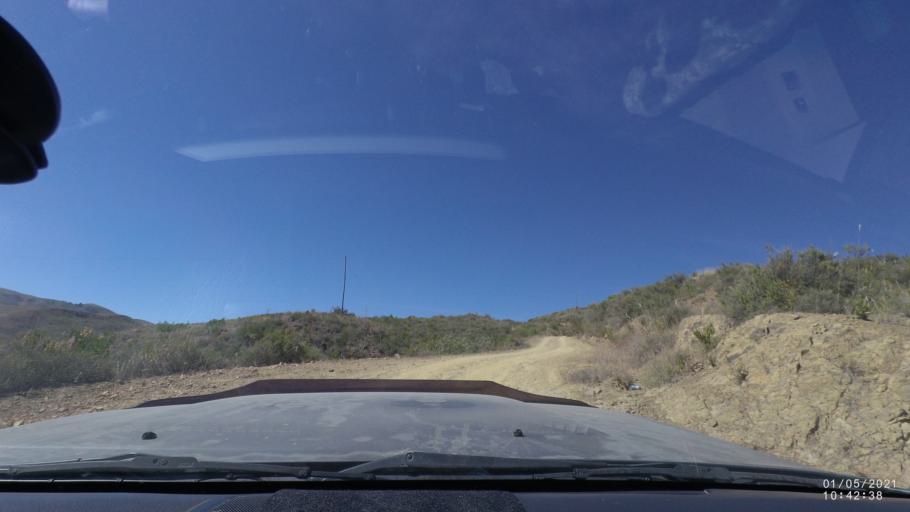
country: BO
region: Cochabamba
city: Capinota
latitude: -17.6129
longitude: -66.1762
